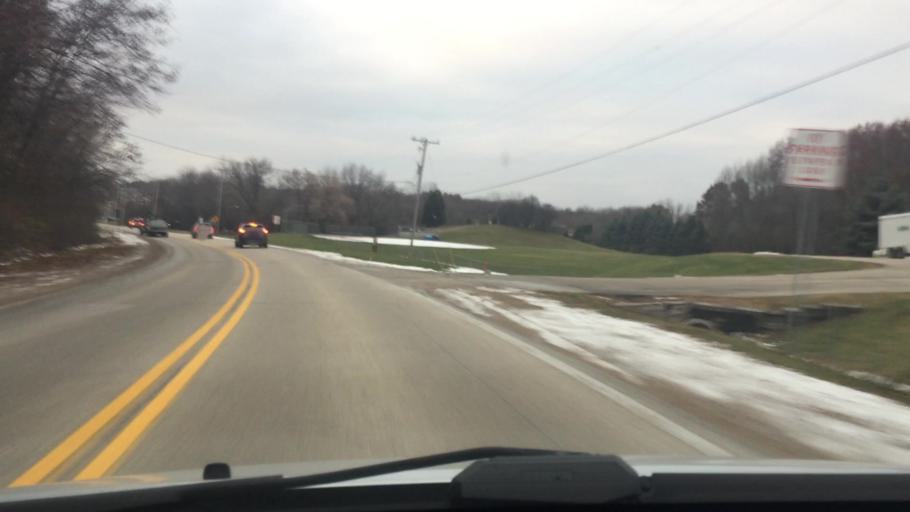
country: US
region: Wisconsin
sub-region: Waukesha County
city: Delafield
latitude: 43.0513
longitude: -88.3605
